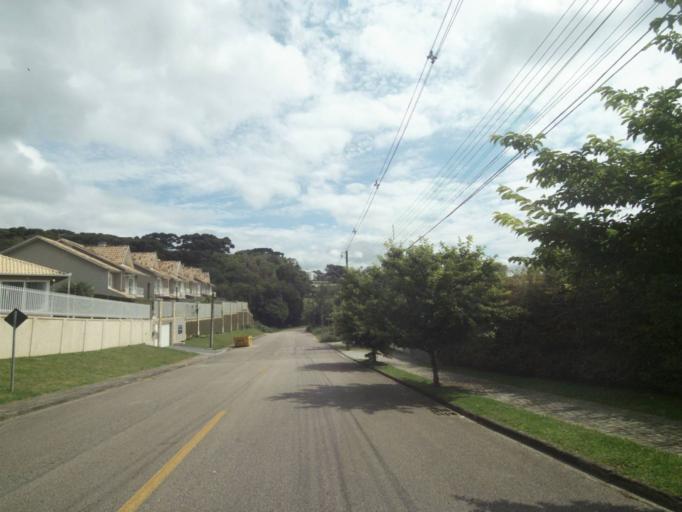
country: BR
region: Parana
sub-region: Curitiba
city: Curitiba
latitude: -25.3806
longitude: -49.2829
